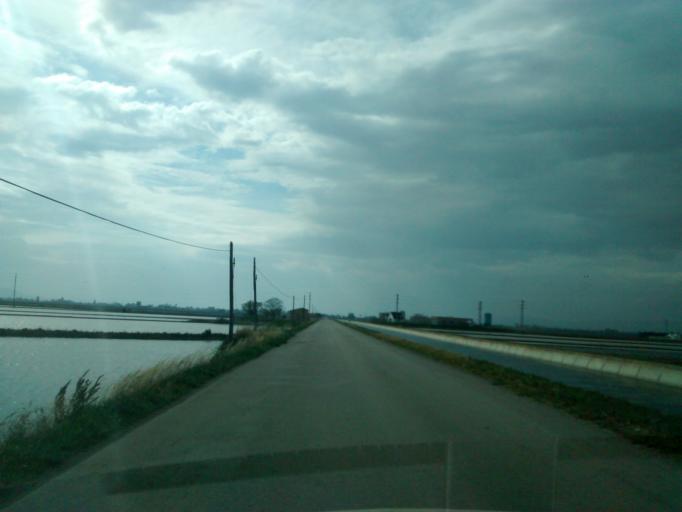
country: ES
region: Catalonia
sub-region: Provincia de Tarragona
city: Deltebre
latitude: 40.6972
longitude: 0.7578
